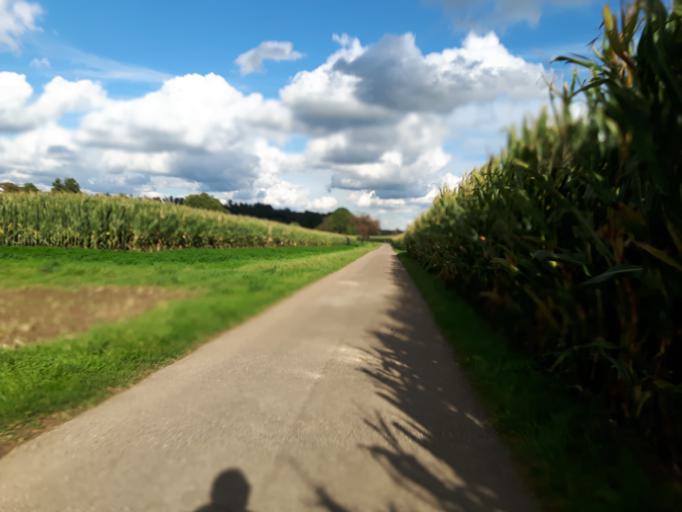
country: DE
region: Baden-Wuerttemberg
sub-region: Regierungsbezirk Stuttgart
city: Bad Wimpfen
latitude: 49.2406
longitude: 9.1352
